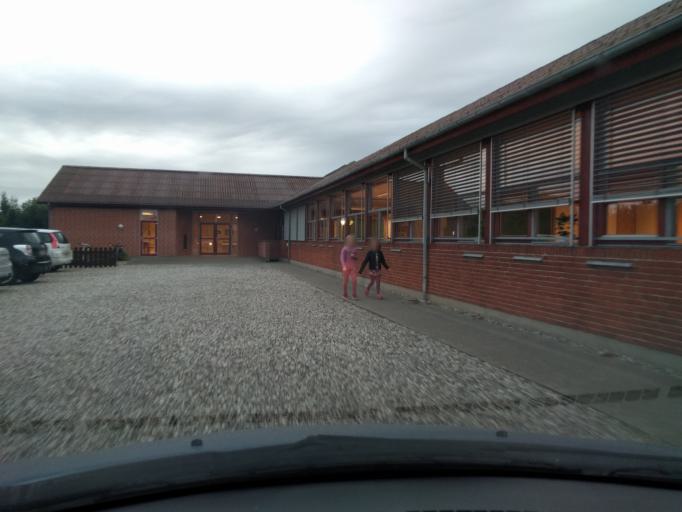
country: DK
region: South Denmark
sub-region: Odense Kommune
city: Bellinge
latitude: 55.3384
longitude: 10.2924
